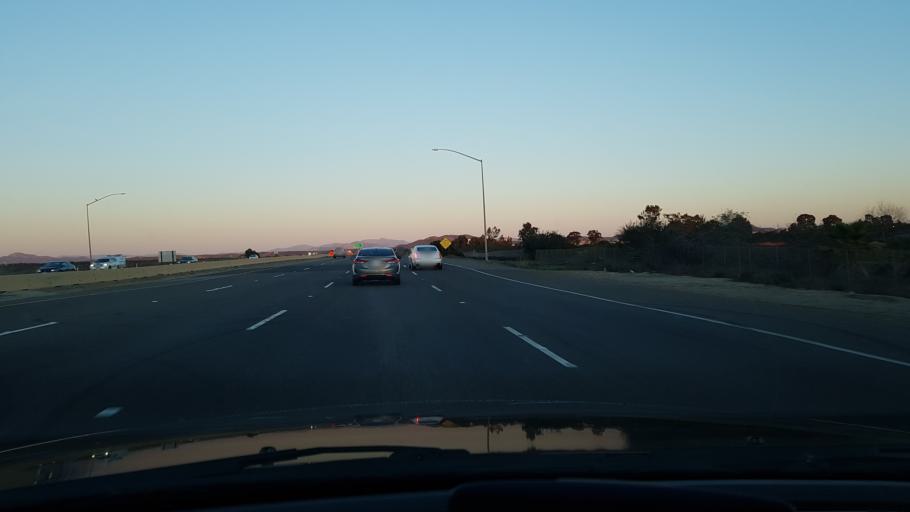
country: US
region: California
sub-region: San Diego County
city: San Diego
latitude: 32.8383
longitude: -117.1486
